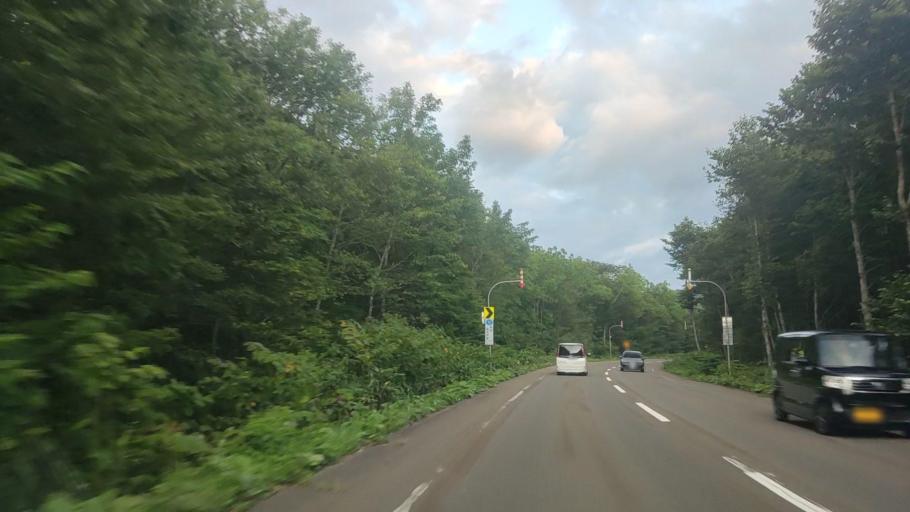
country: JP
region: Hokkaido
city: Ashibetsu
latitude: 43.3751
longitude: 142.2225
